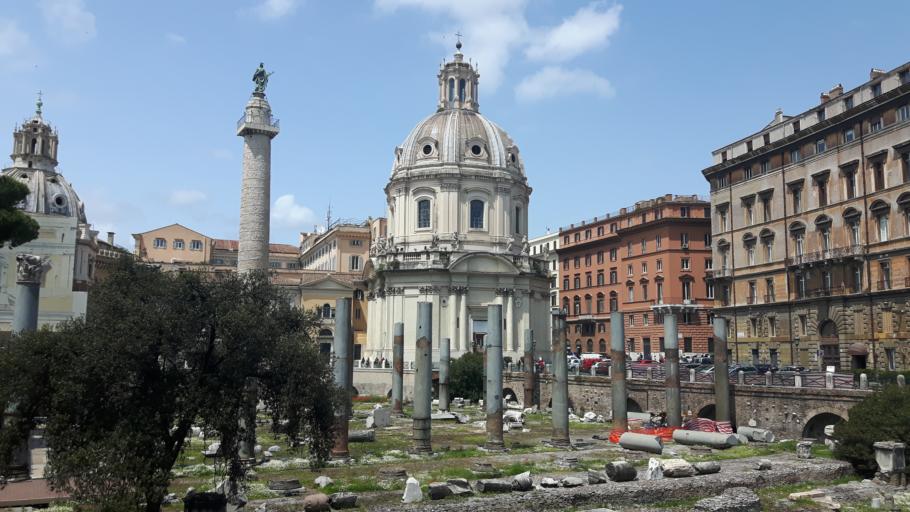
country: IT
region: Latium
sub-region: Citta metropolitana di Roma Capitale
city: Rome
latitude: 41.8952
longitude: 12.4850
